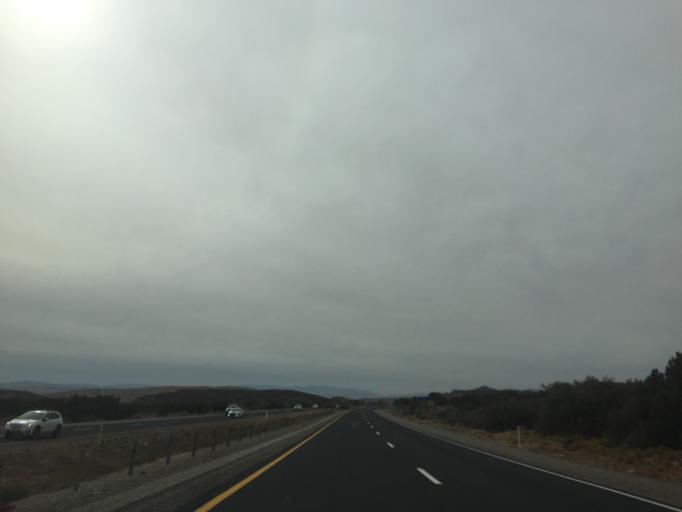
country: US
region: Utah
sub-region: Washington County
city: Toquerville
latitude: 37.2579
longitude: -113.3327
